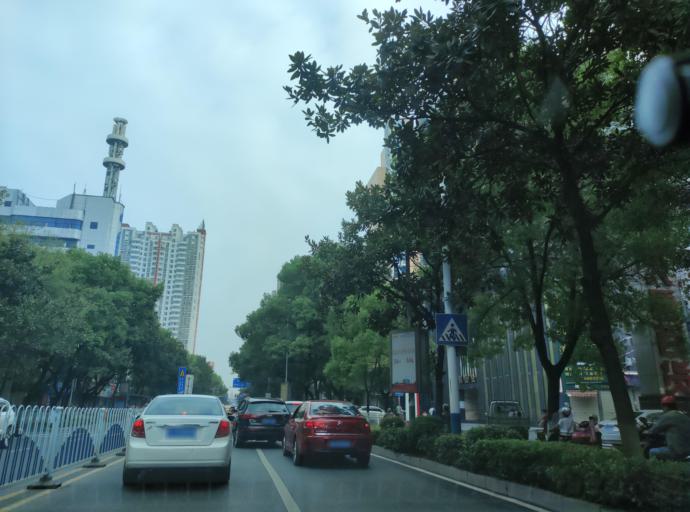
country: CN
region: Jiangxi Sheng
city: Pingxiang
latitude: 27.6426
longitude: 113.8407
